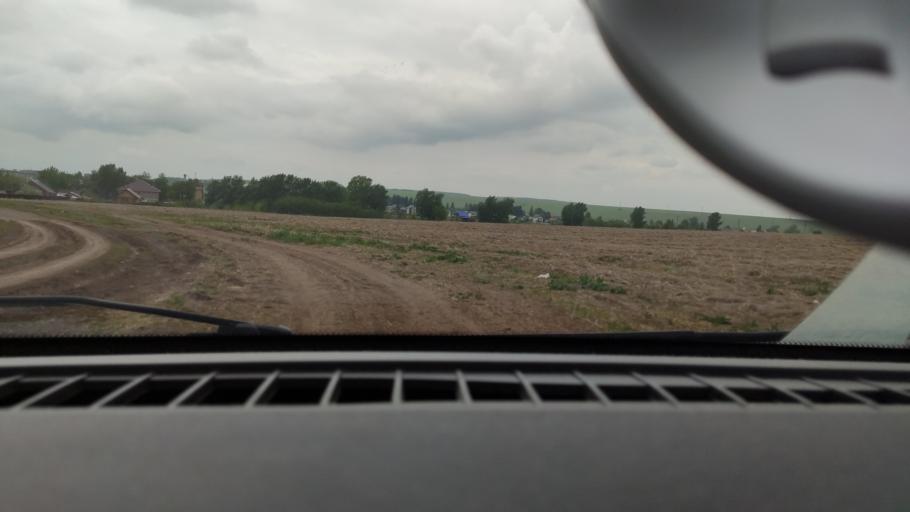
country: RU
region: Perm
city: Gamovo
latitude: 57.8740
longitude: 56.1077
